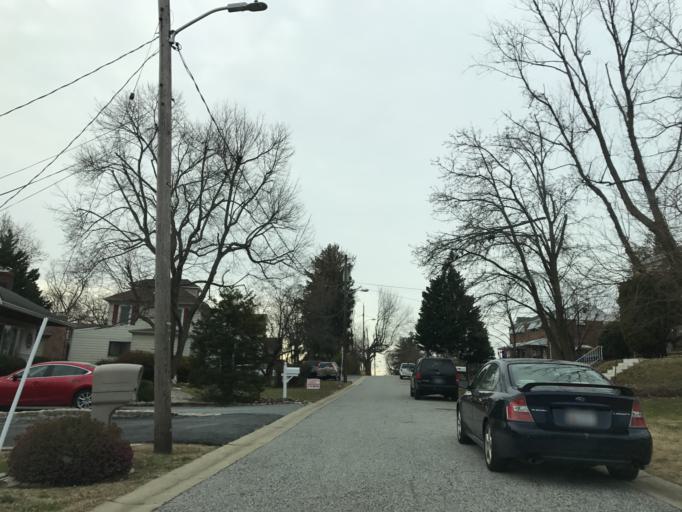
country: US
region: Maryland
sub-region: Baltimore County
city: Overlea
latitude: 39.3613
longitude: -76.5363
